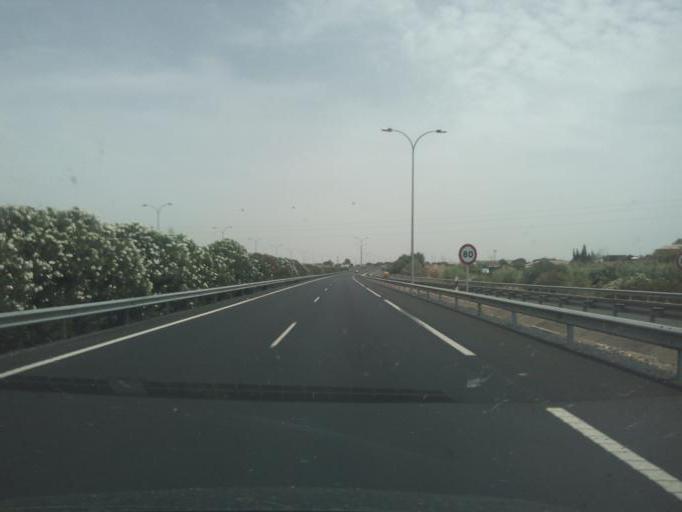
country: ES
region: Andalusia
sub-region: Provincia de Huelva
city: Bollullos par del Condado
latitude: 37.3557
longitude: -6.5534
